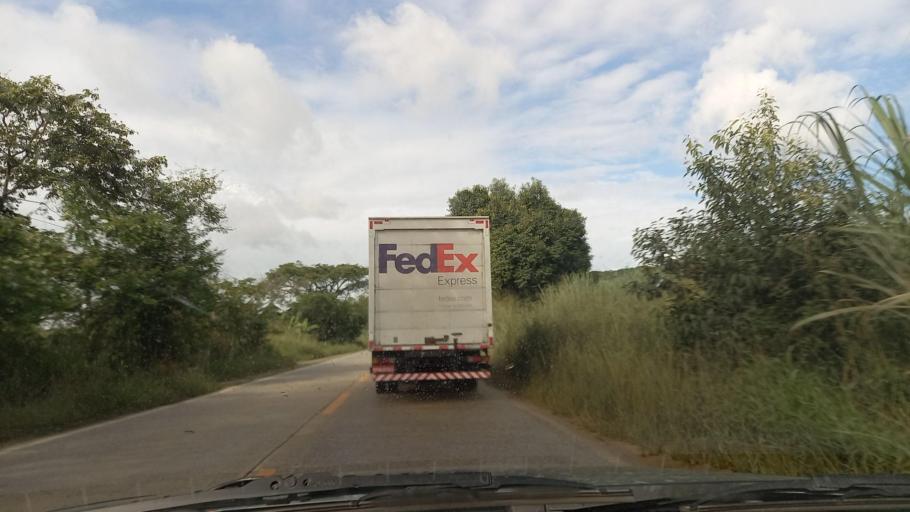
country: BR
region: Pernambuco
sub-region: Catende
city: Catende
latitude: -8.6932
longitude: -35.6820
